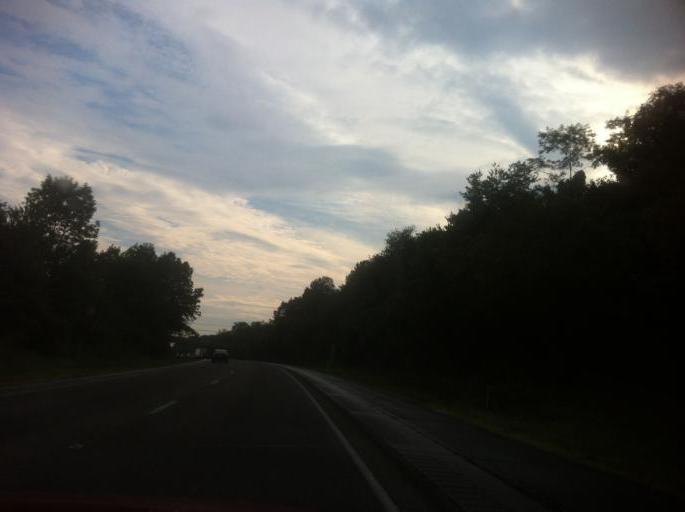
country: US
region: Pennsylvania
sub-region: Clarion County
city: Knox
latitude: 41.1946
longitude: -79.5854
